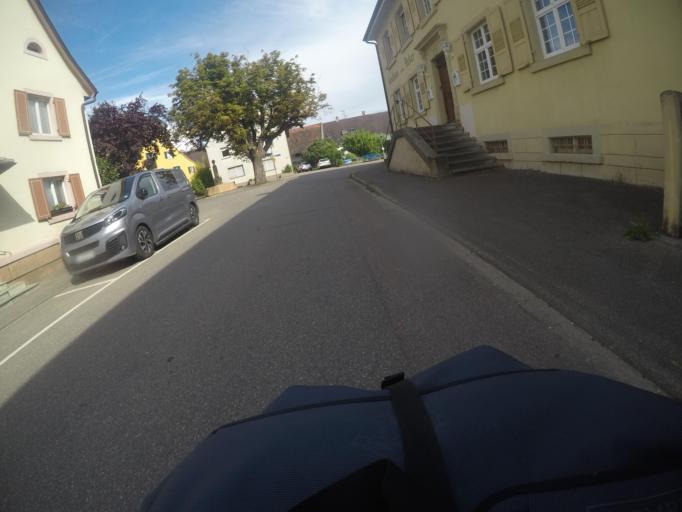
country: DE
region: Baden-Wuerttemberg
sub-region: Freiburg Region
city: Efringen-Kirchen
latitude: 47.6471
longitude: 7.5682
